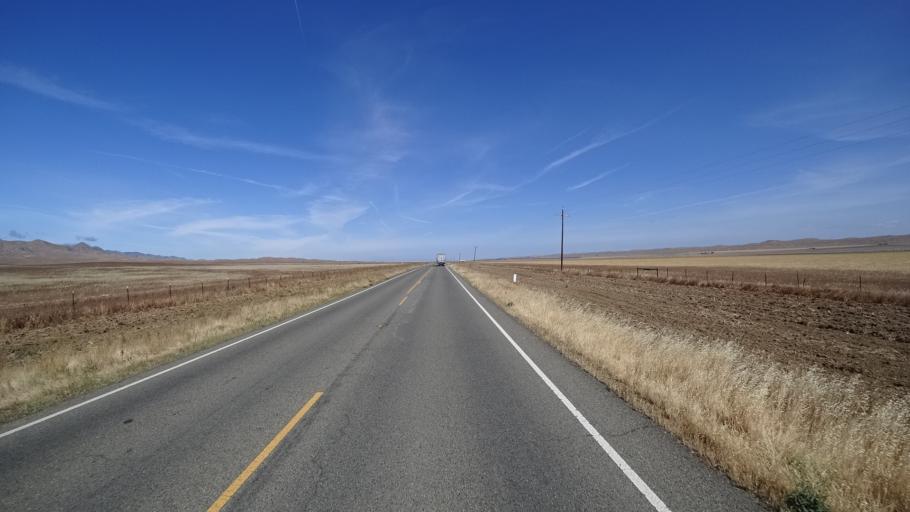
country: US
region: California
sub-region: Kings County
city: Avenal
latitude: 35.9273
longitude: -120.0785
